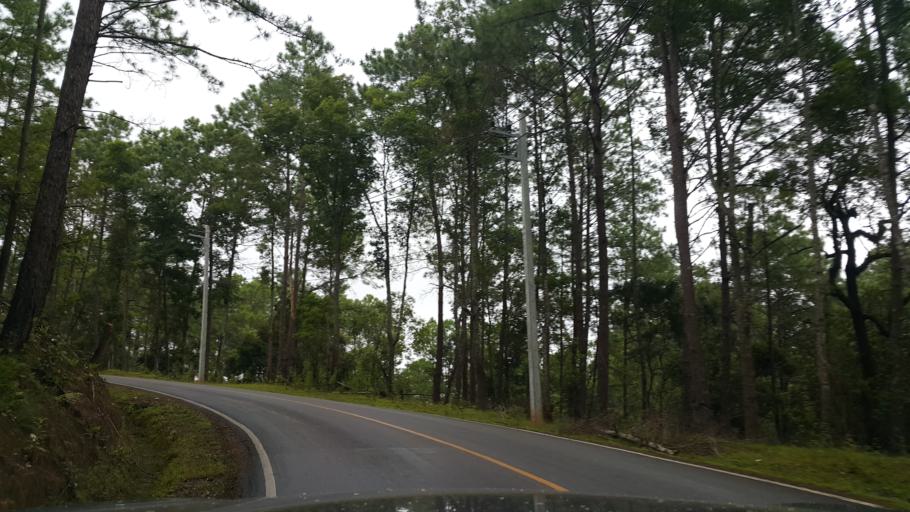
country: TH
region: Chiang Mai
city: Samoeng
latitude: 18.8877
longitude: 98.5309
